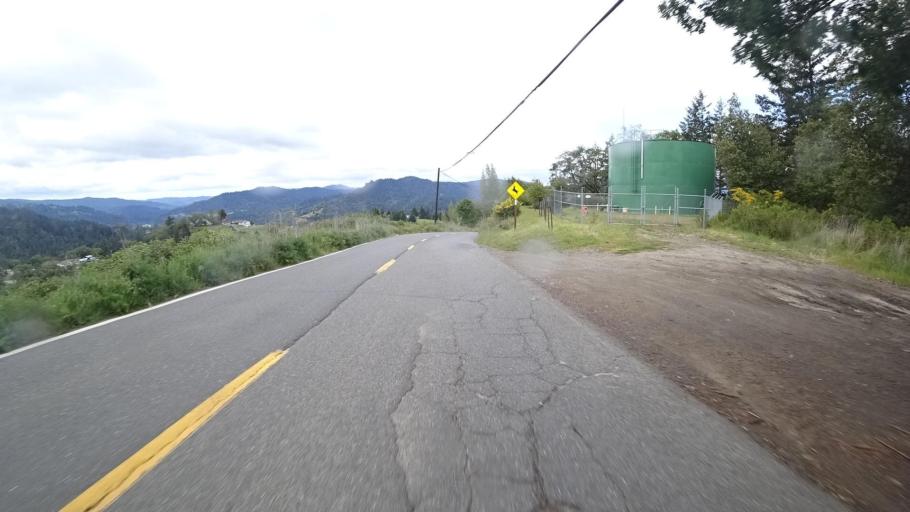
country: US
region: California
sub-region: Humboldt County
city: Redway
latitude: 40.1108
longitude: -123.7810
